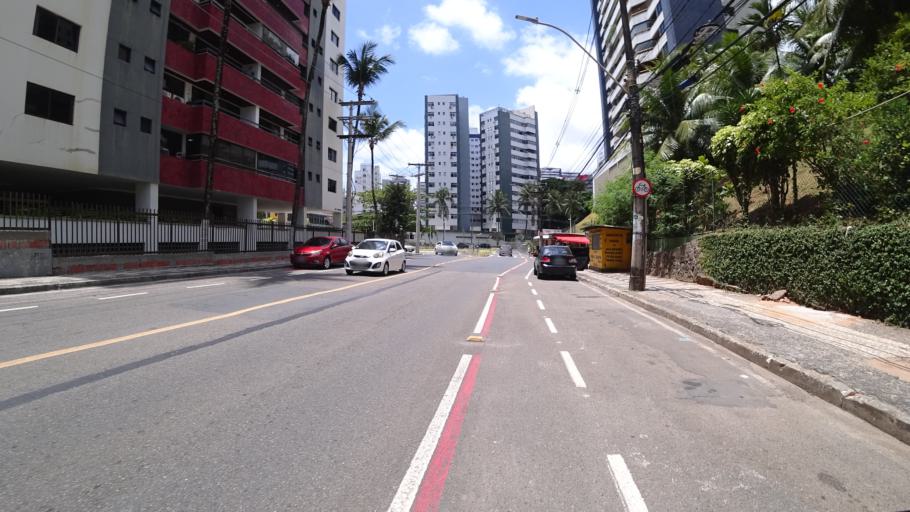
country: BR
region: Bahia
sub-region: Salvador
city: Salvador
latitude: -13.0037
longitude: -38.4607
